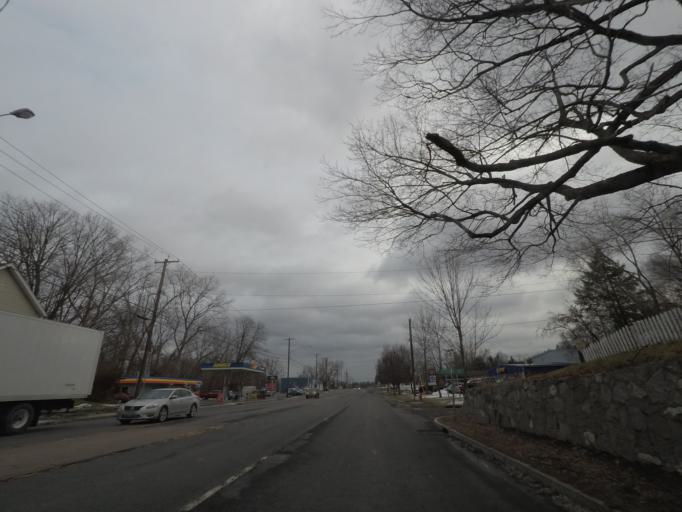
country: US
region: New York
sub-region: Rensselaer County
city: Hampton Manor
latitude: 42.6134
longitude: -73.7286
